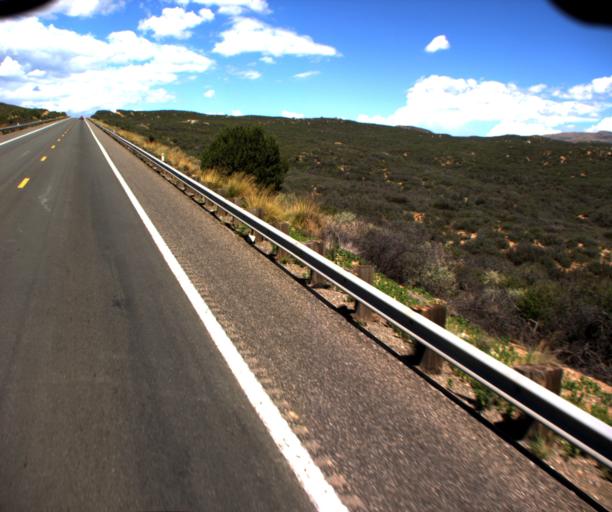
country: US
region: Arizona
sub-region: Yavapai County
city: Dewey-Humboldt
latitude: 34.5322
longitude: -112.1221
